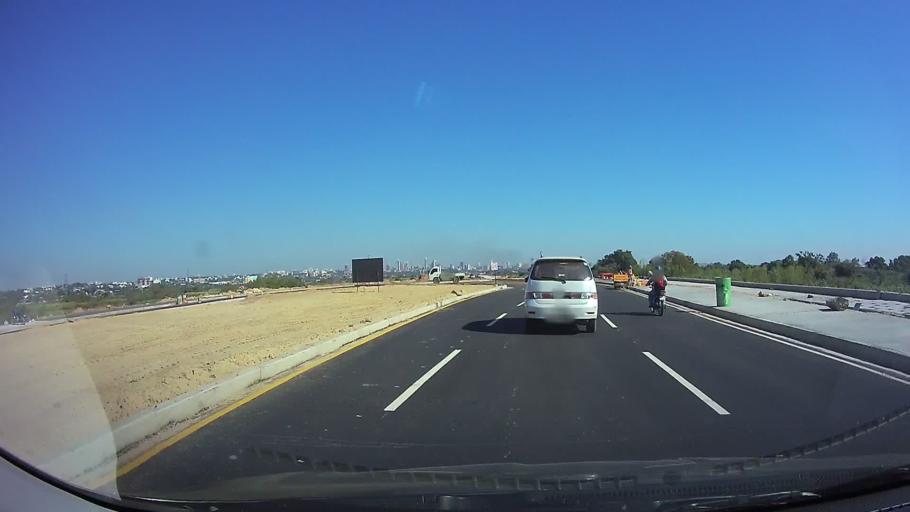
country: PY
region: Asuncion
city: Asuncion
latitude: -25.2524
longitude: -57.6057
